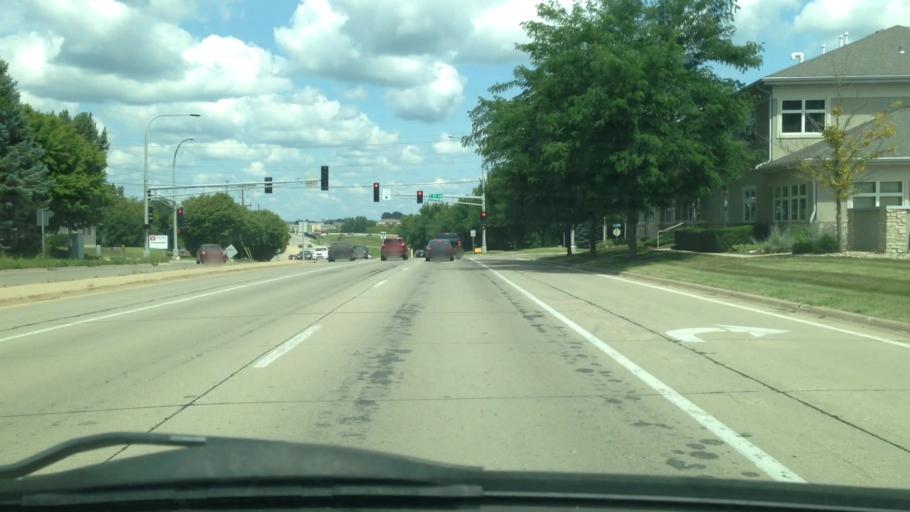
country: US
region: Minnesota
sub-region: Olmsted County
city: Rochester
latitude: 44.0318
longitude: -92.5164
